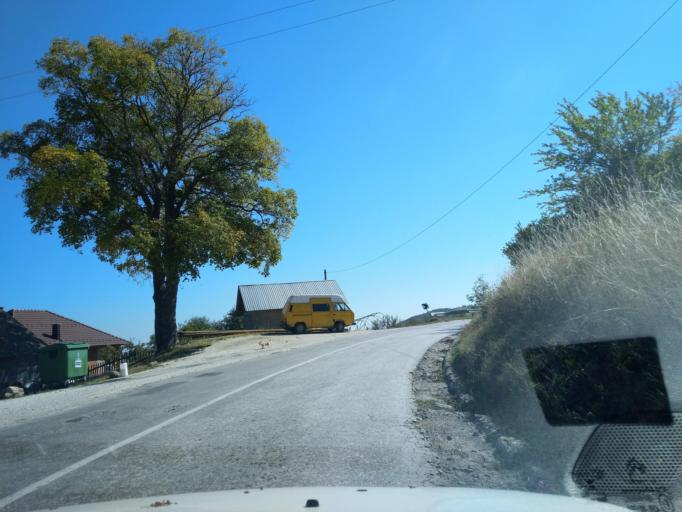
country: RS
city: Sokolovica
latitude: 43.2611
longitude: 20.2330
